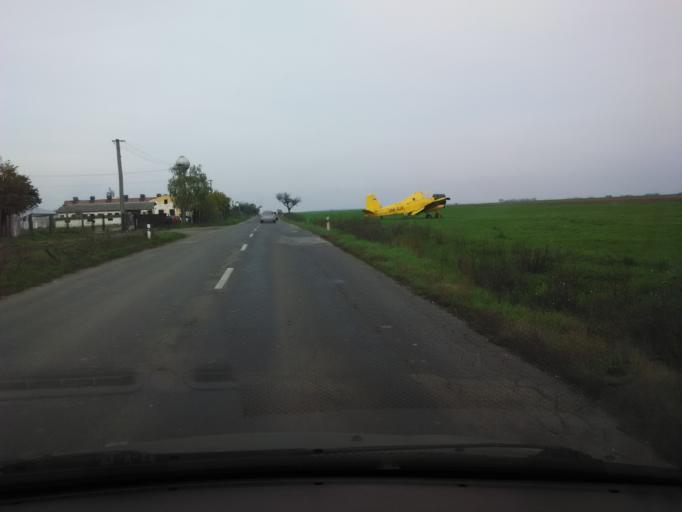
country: SK
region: Nitriansky
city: Levice
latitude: 48.1163
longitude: 18.5303
